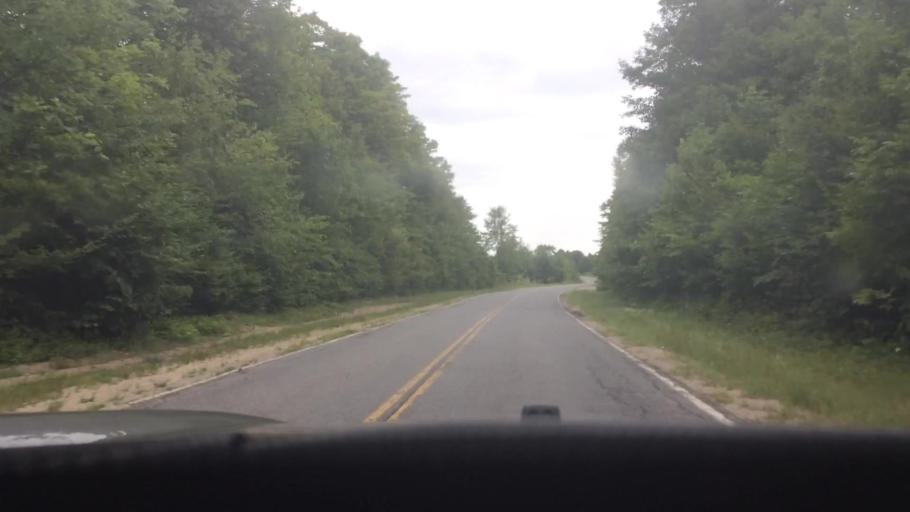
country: US
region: New York
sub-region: St. Lawrence County
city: Hannawa Falls
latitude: 44.5716
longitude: -74.9072
